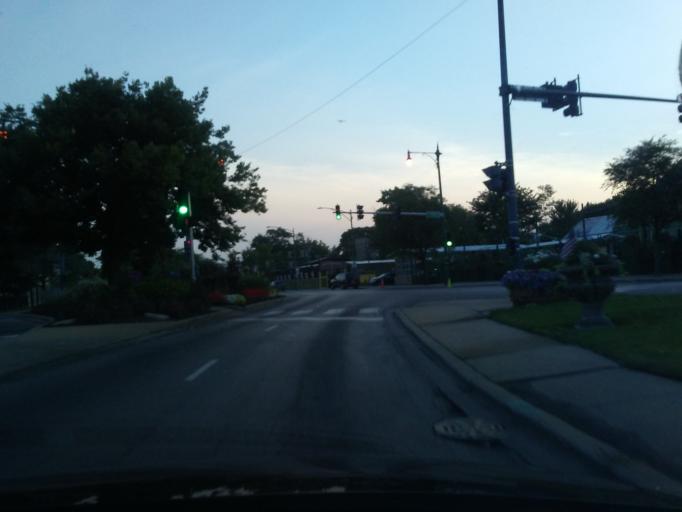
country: US
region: Illinois
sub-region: Cook County
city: Evanston
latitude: 41.9864
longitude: -87.6697
